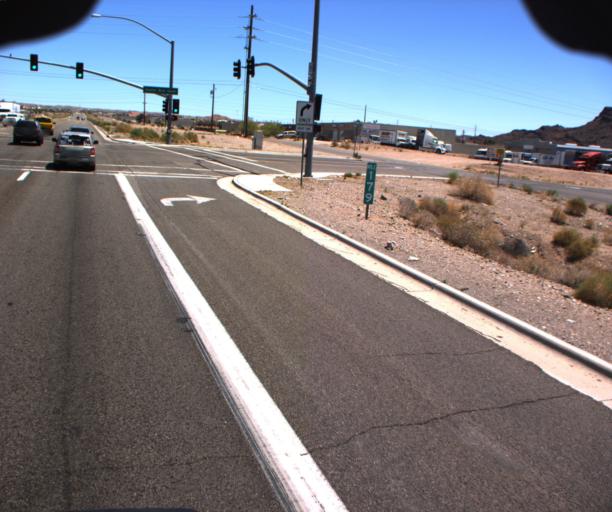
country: US
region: Arizona
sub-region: Mohave County
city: Lake Havasu City
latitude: 34.4544
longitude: -114.2981
